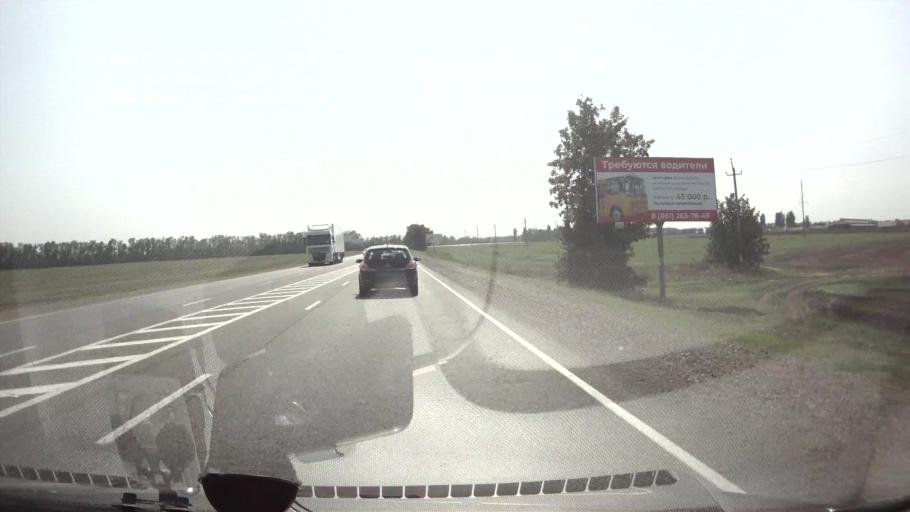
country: RU
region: Krasnodarskiy
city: Vasyurinskaya
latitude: 45.1037
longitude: 39.3873
